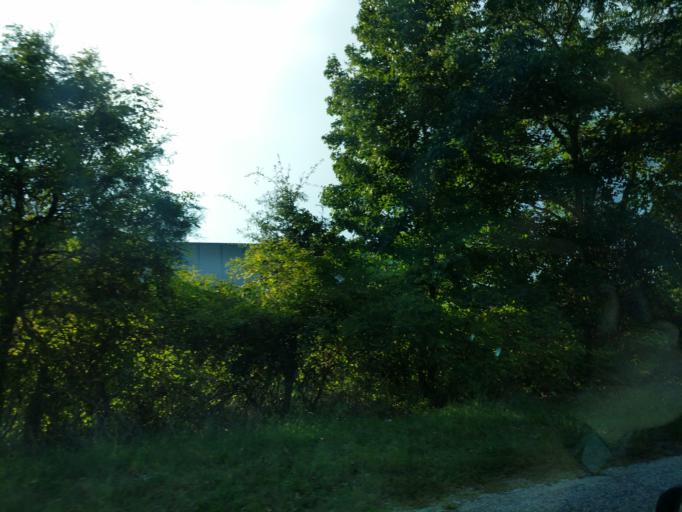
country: US
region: South Carolina
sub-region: Anderson County
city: Piedmont
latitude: 34.6962
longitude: -82.5028
